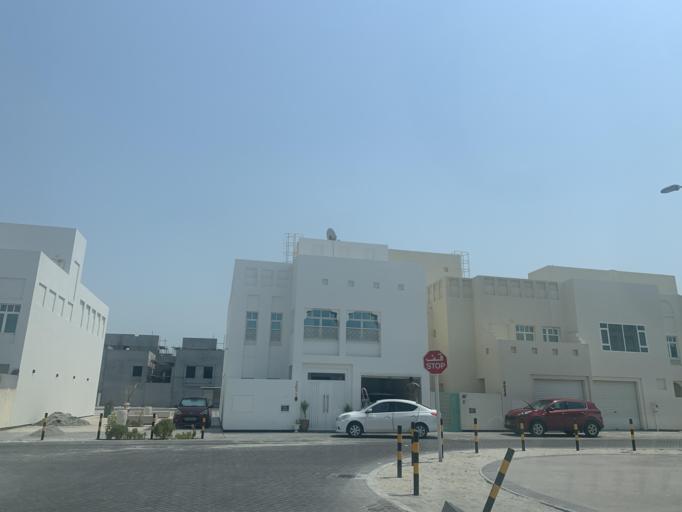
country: BH
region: Muharraq
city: Al Hadd
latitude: 26.2402
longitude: 50.6650
